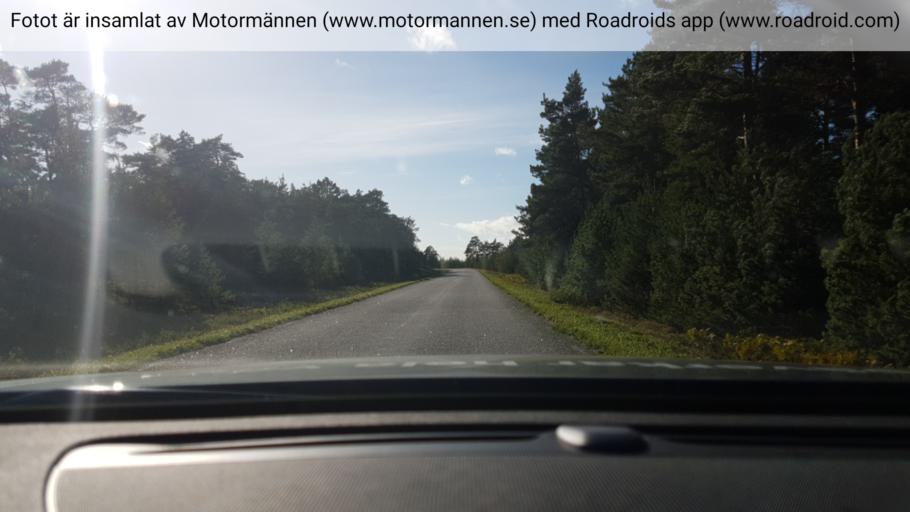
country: SE
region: Gotland
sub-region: Gotland
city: Slite
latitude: 57.8605
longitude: 18.8324
